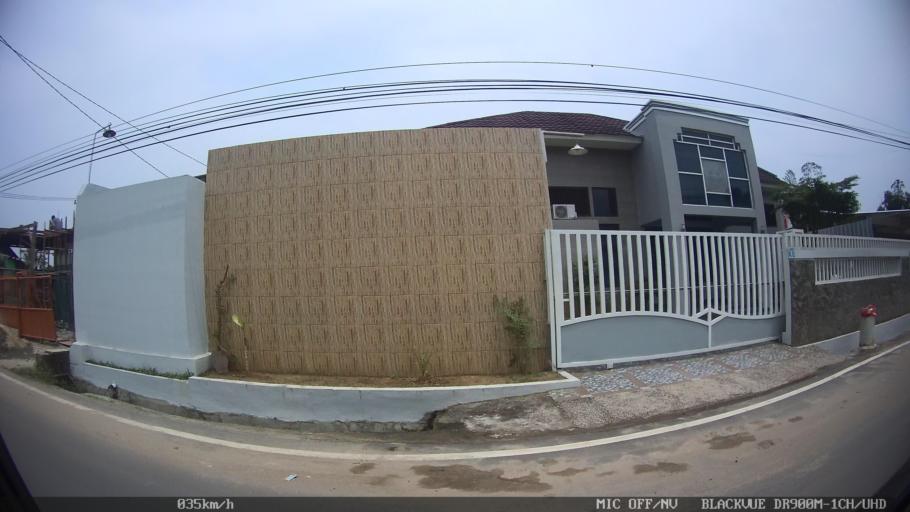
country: ID
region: Lampung
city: Kedaton
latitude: -5.3963
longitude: 105.3159
